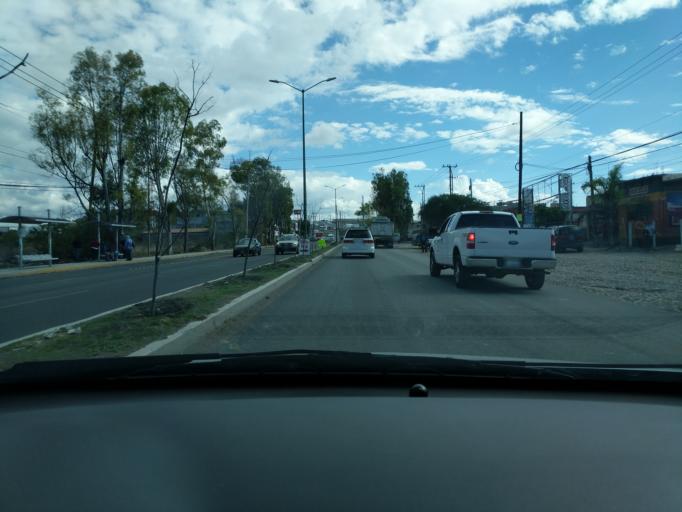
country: MX
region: Queretaro
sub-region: El Marques
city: General Lazaro Cardenas (El Colorado)
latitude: 20.5758
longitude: -100.2575
